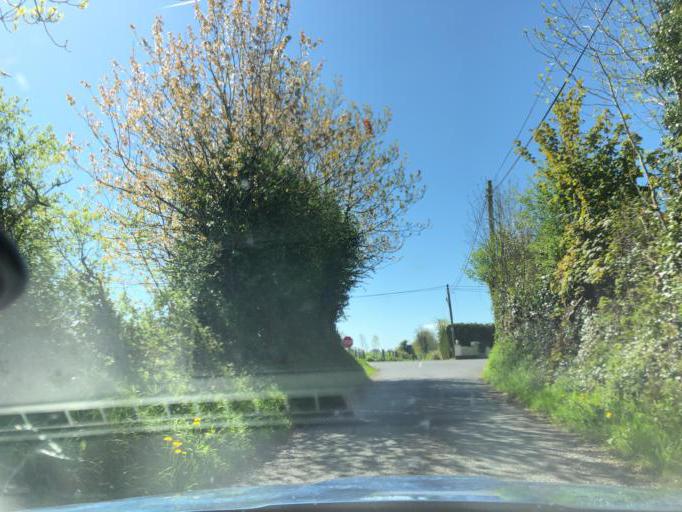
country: IE
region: Connaught
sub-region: County Galway
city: Portumna
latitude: 53.1237
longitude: -8.3309
